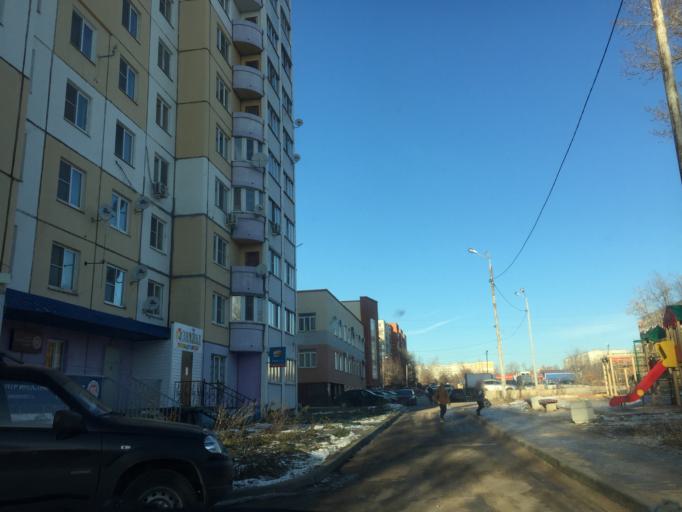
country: RU
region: Tula
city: Tula
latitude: 54.2124
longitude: 37.6039
